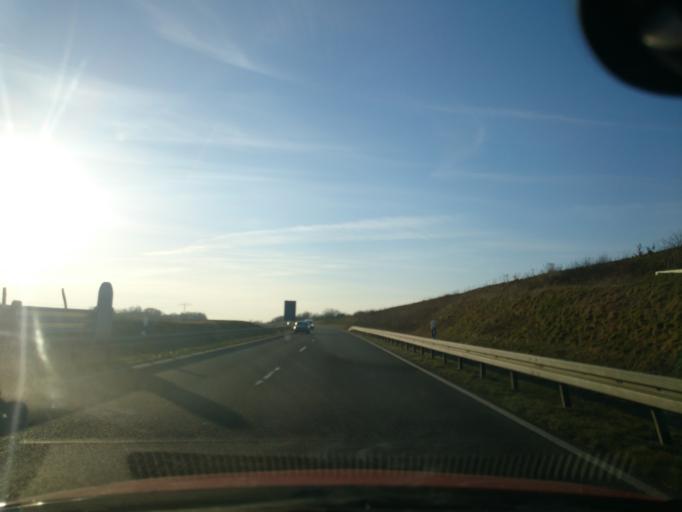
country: DE
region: Mecklenburg-Vorpommern
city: Stralsund
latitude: 54.2963
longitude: 13.0440
